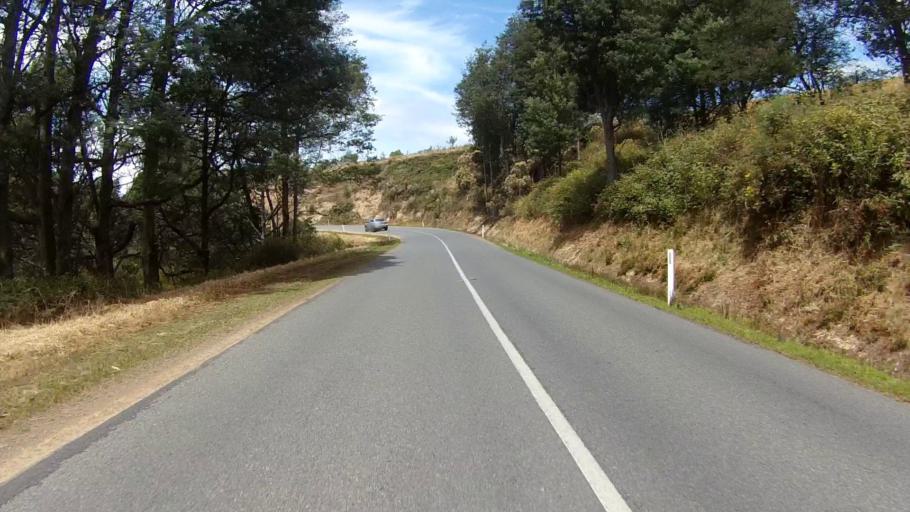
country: AU
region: Tasmania
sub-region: Kingborough
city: Kettering
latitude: -43.1055
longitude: 147.2264
